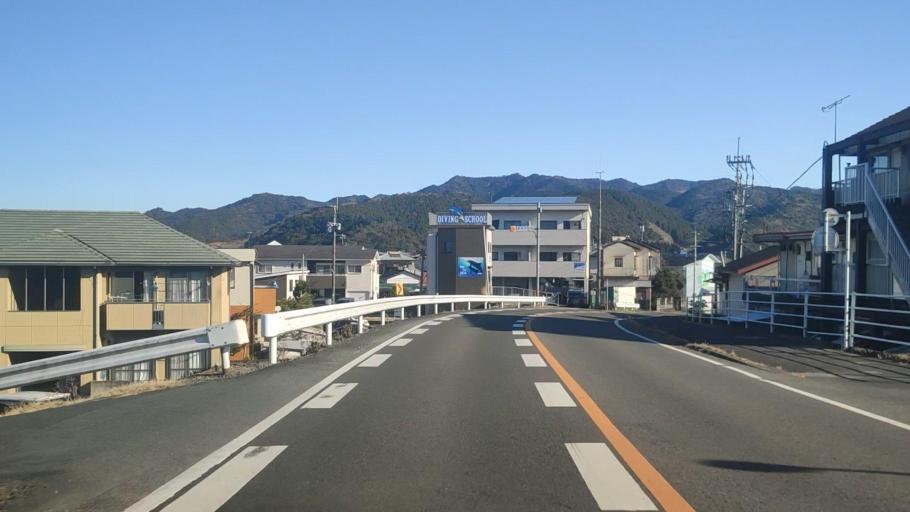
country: JP
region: Miyazaki
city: Nobeoka
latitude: 32.6140
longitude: 131.6905
